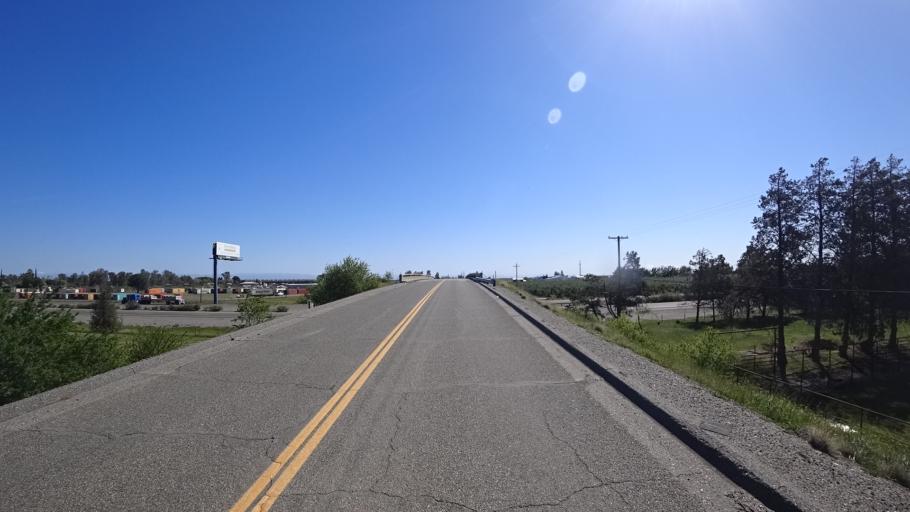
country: US
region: California
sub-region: Glenn County
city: Orland
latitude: 39.6970
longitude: -122.2062
